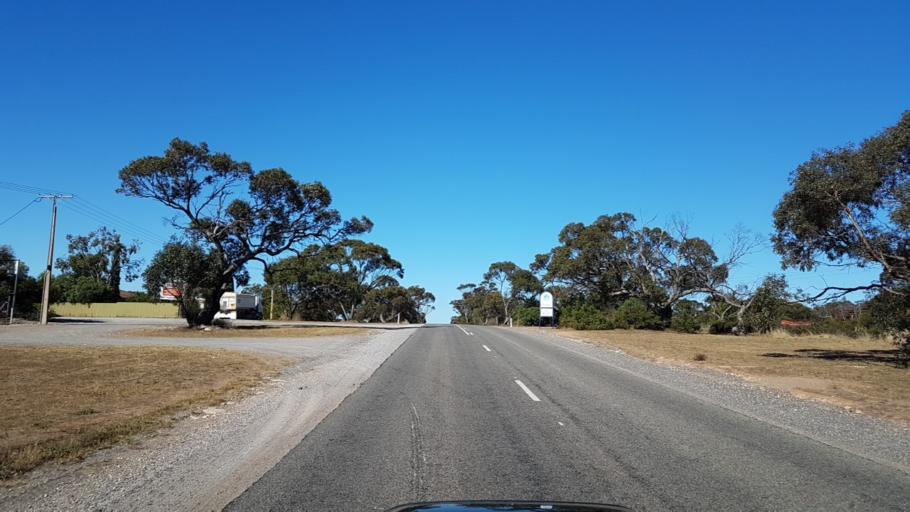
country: AU
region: South Australia
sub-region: Yorke Peninsula
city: Port Victoria
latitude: -34.7643
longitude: 137.6042
